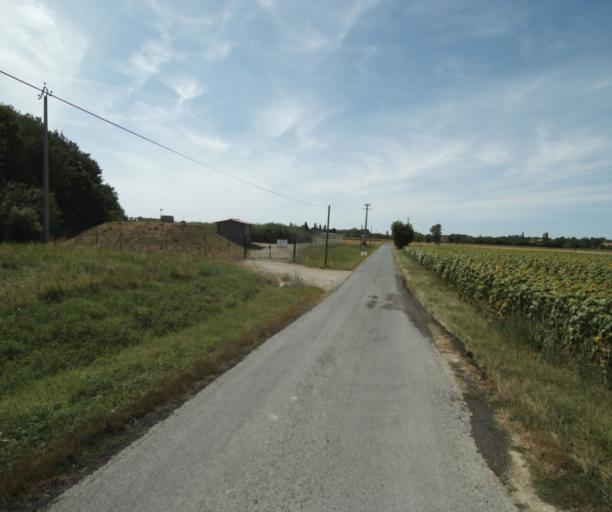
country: FR
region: Midi-Pyrenees
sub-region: Departement du Tarn
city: Puylaurens
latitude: 43.5157
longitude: 2.0215
